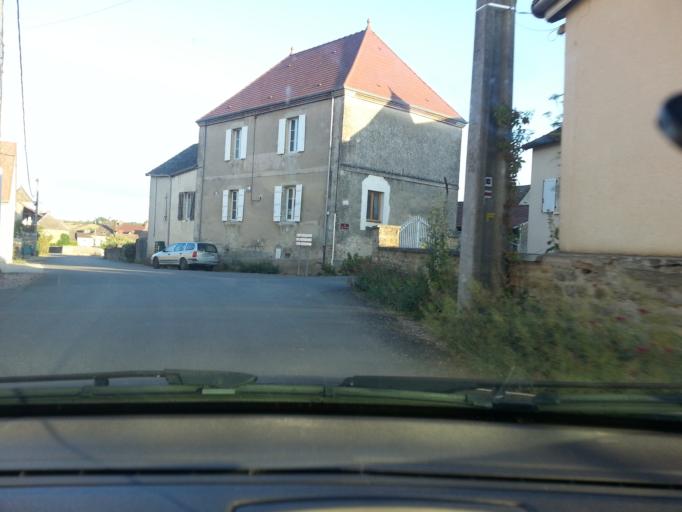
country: FR
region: Bourgogne
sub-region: Departement de Saone-et-Loire
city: Buxy
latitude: 46.7575
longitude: 4.6880
